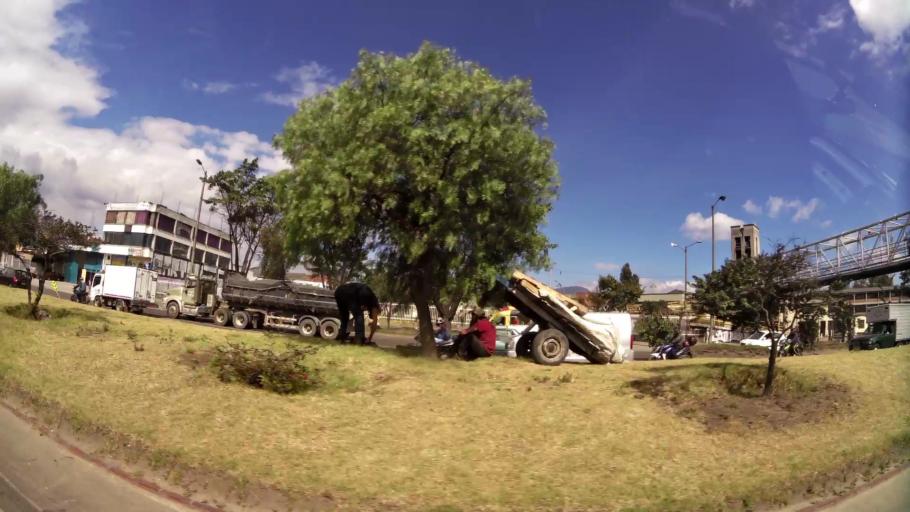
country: CO
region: Bogota D.C.
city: Bogota
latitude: 4.6134
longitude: -74.1408
